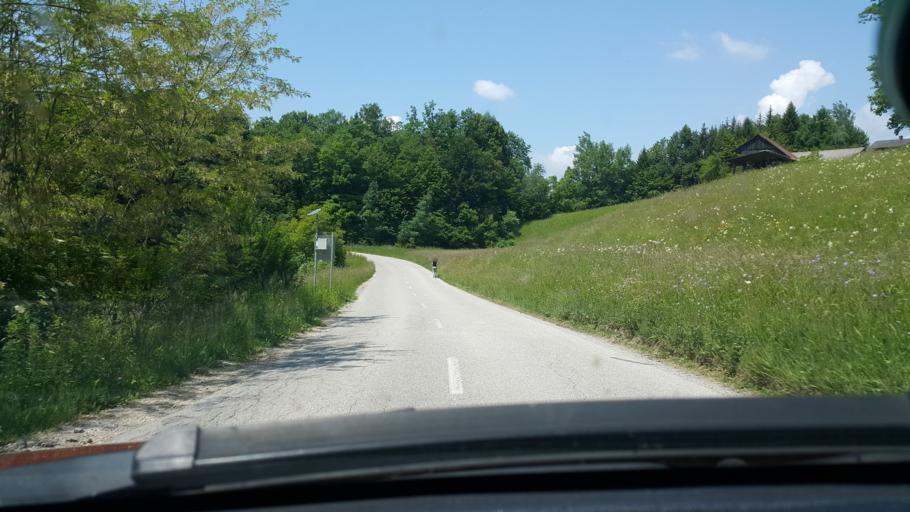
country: SI
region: Novo Mesto
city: Novo Mesto
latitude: 45.7643
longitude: 15.1622
